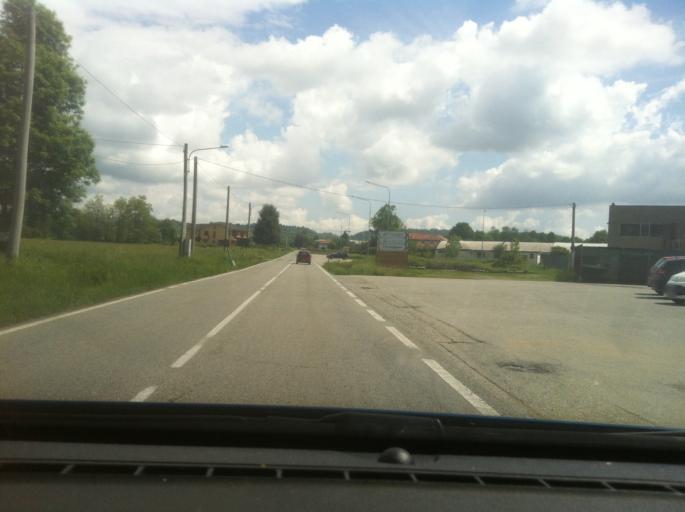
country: IT
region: Piedmont
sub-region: Provincia di Torino
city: Castellamonte
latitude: 45.3893
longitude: 7.7261
